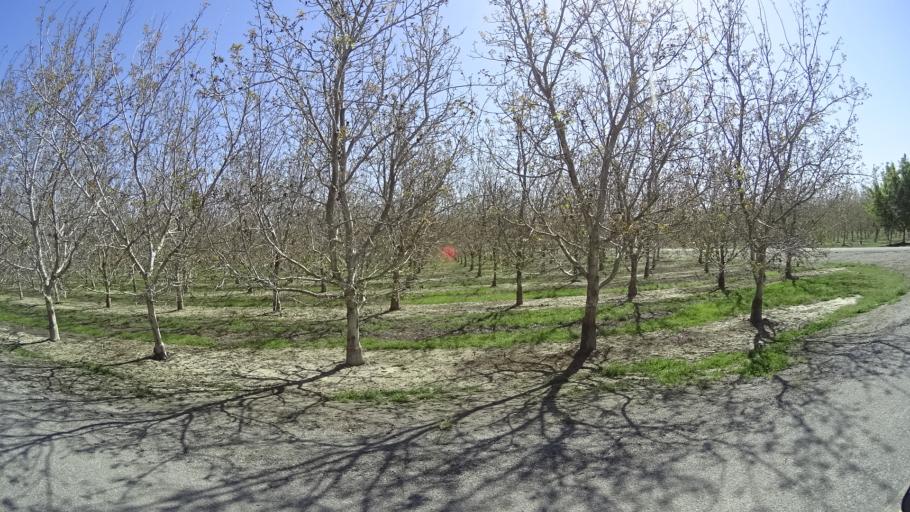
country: US
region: California
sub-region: Glenn County
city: Hamilton City
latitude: 39.7219
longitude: -122.0213
